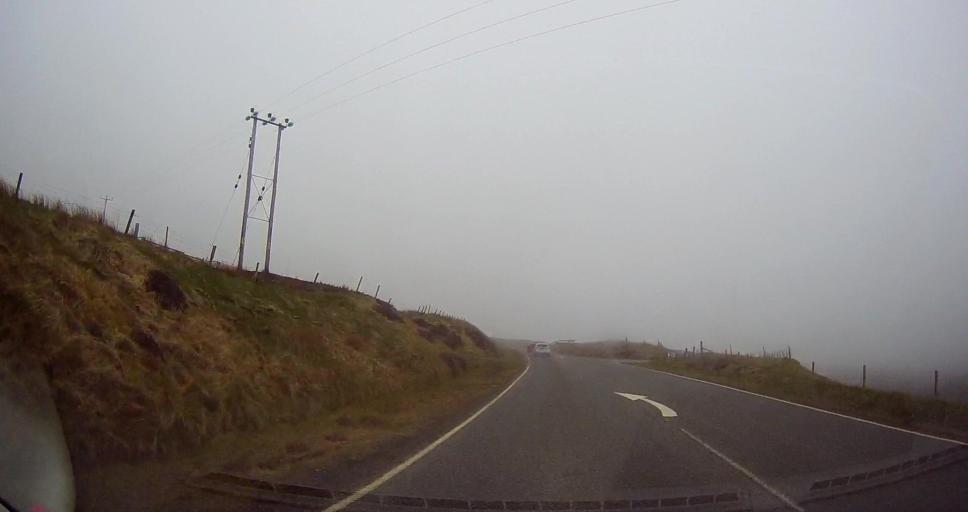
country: GB
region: Scotland
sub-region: Shetland Islands
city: Lerwick
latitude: 60.1394
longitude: -1.2348
